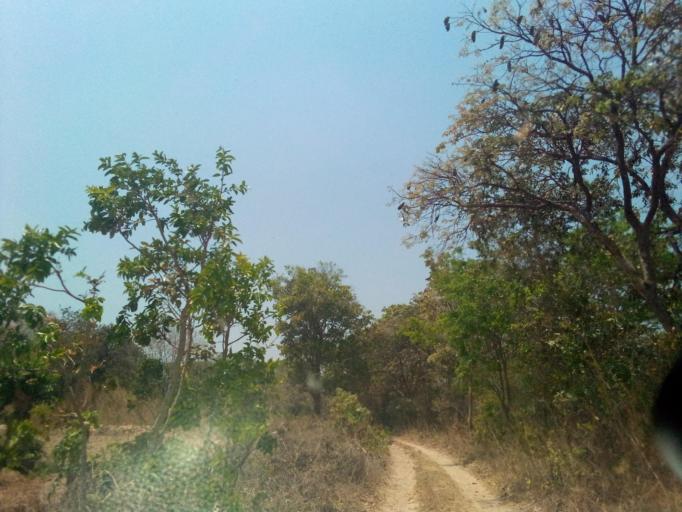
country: ZM
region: Copperbelt
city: Kataba
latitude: -12.2539
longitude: 30.3868
